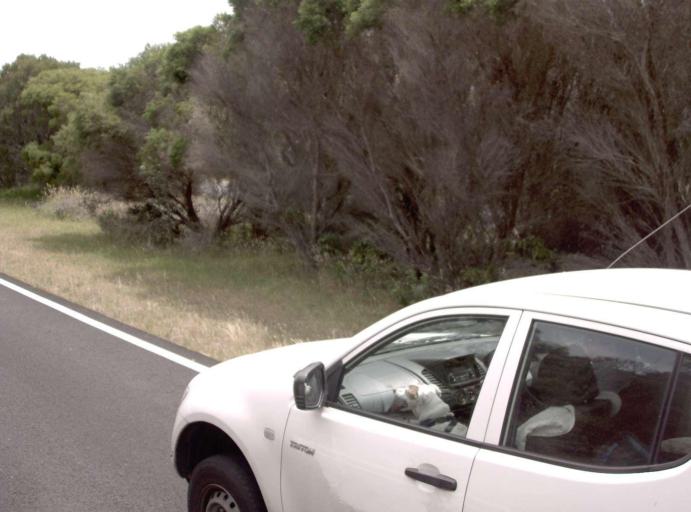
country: AU
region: Victoria
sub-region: Mornington Peninsula
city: McCrae
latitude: -38.3475
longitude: 144.9407
